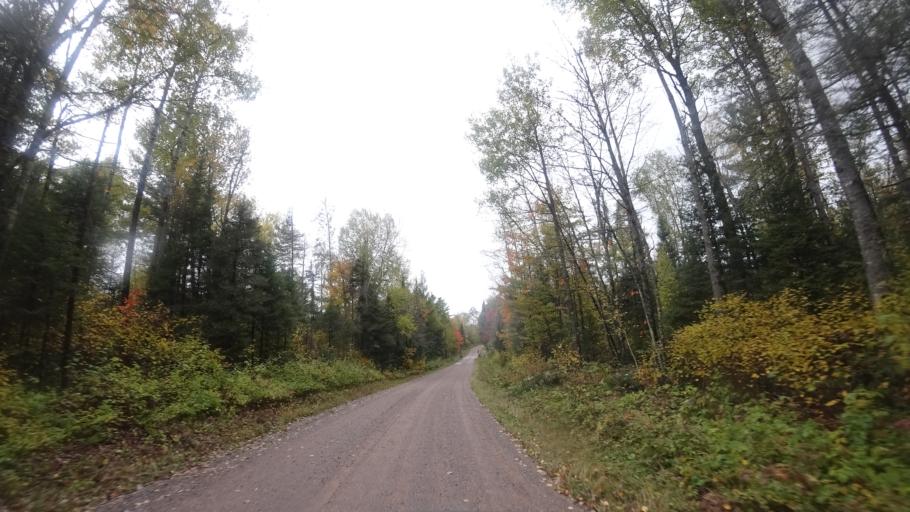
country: US
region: Wisconsin
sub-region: Sawyer County
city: Little Round Lake
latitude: 46.0500
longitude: -90.9934
